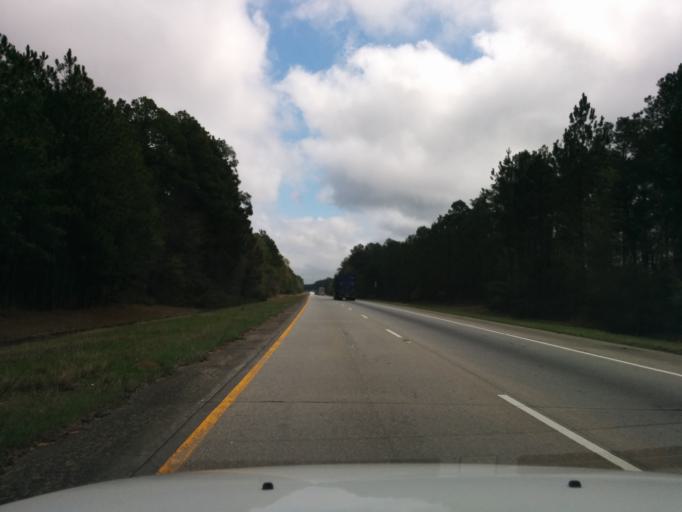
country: US
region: Georgia
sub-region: Emanuel County
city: Swainsboro
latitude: 32.4106
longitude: -82.3647
